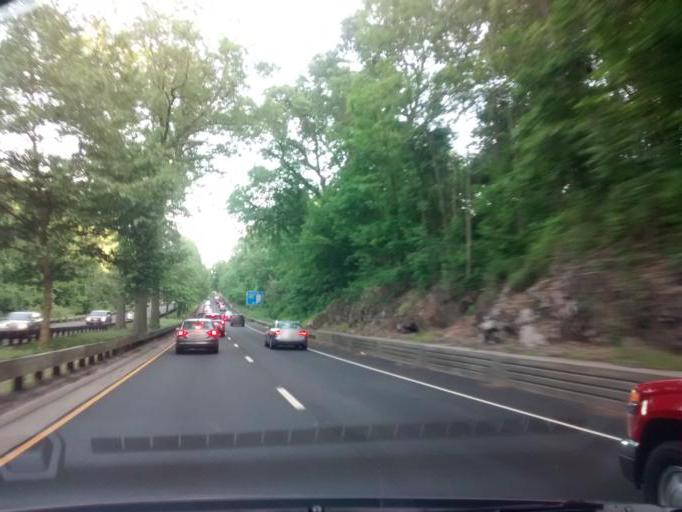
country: US
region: Connecticut
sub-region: Fairfield County
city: Glenville
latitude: 41.0525
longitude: -73.6732
